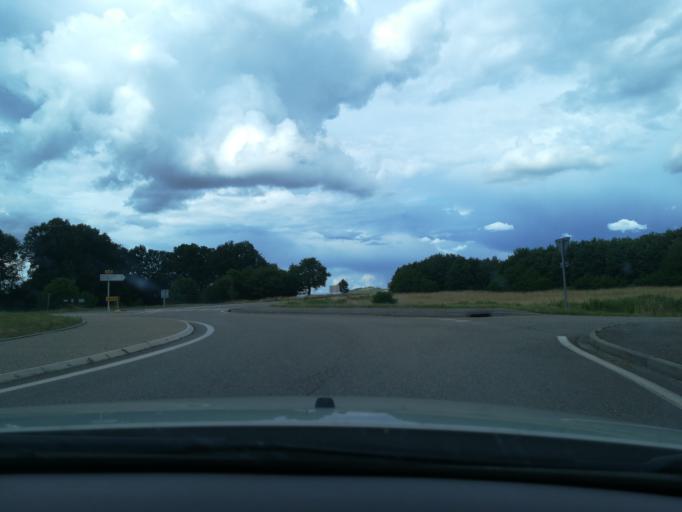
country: FR
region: Alsace
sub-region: Departement du Bas-Rhin
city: Steinbourg
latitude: 48.7805
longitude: 7.4085
